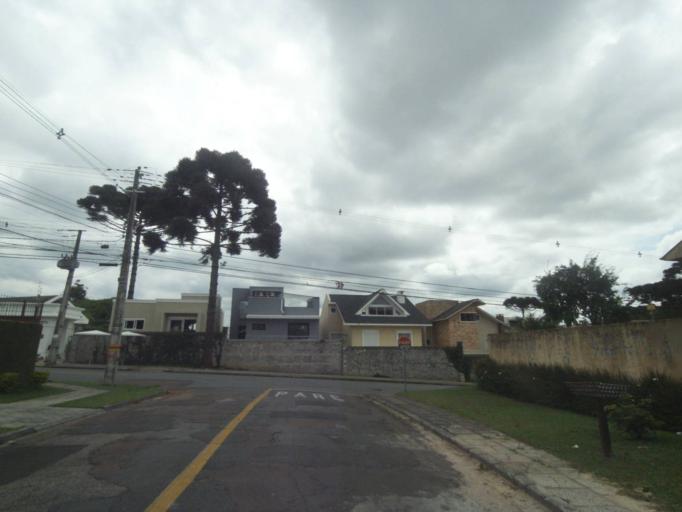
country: BR
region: Parana
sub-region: Curitiba
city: Curitiba
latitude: -25.3898
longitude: -49.2888
